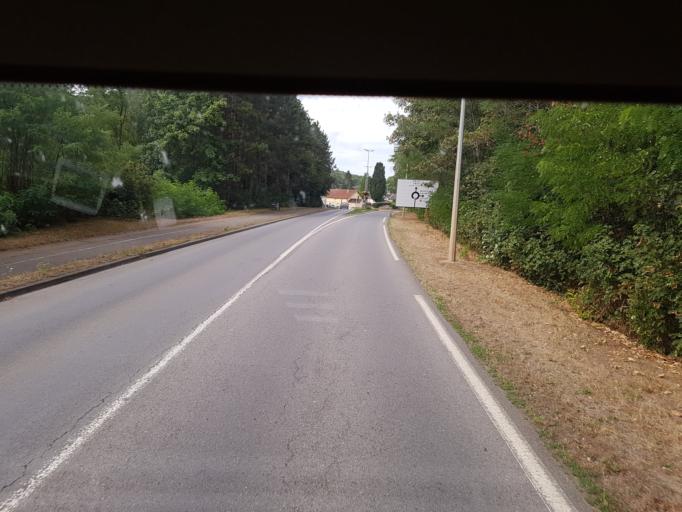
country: FR
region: Lorraine
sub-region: Departement de la Moselle
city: Moyeuvre-Grande
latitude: 49.2500
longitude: 6.0518
